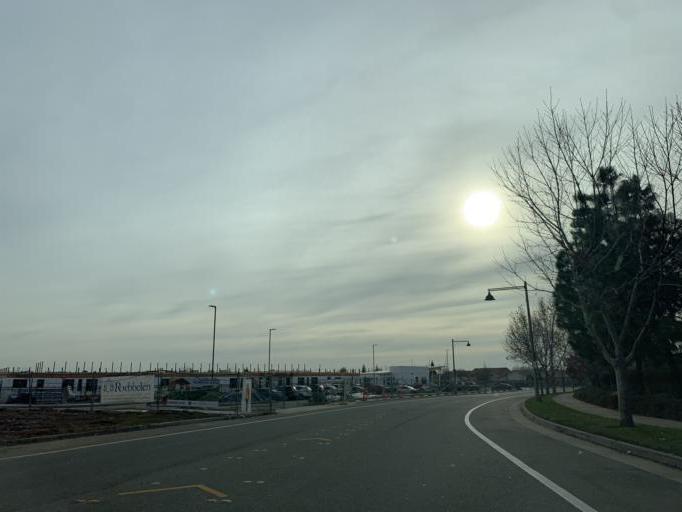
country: US
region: California
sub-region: Placer County
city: Lincoln
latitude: 38.8651
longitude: -121.3118
